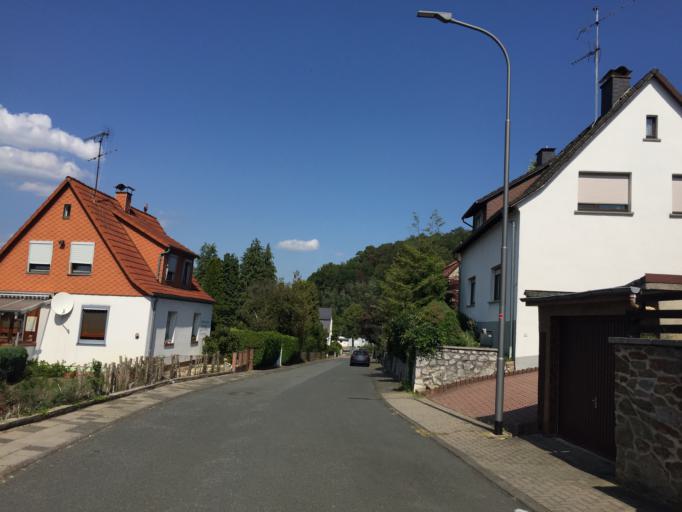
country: DE
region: Hesse
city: Solms
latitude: 50.5192
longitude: 8.4113
